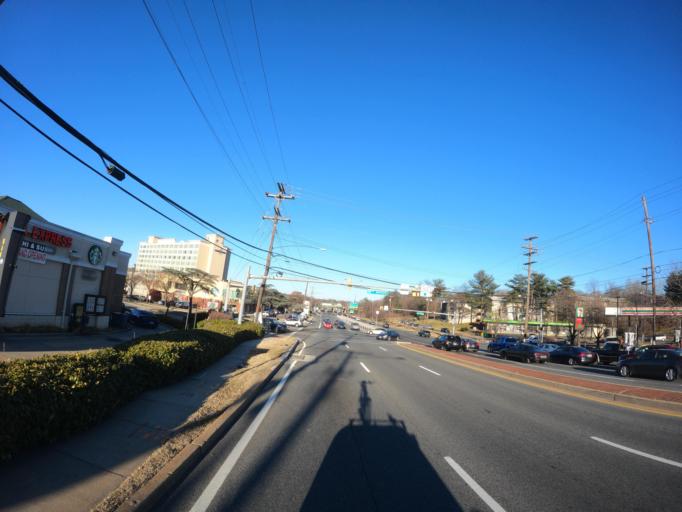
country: US
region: Maryland
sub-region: Prince George's County
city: Lanham
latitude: 38.9576
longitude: -76.8698
